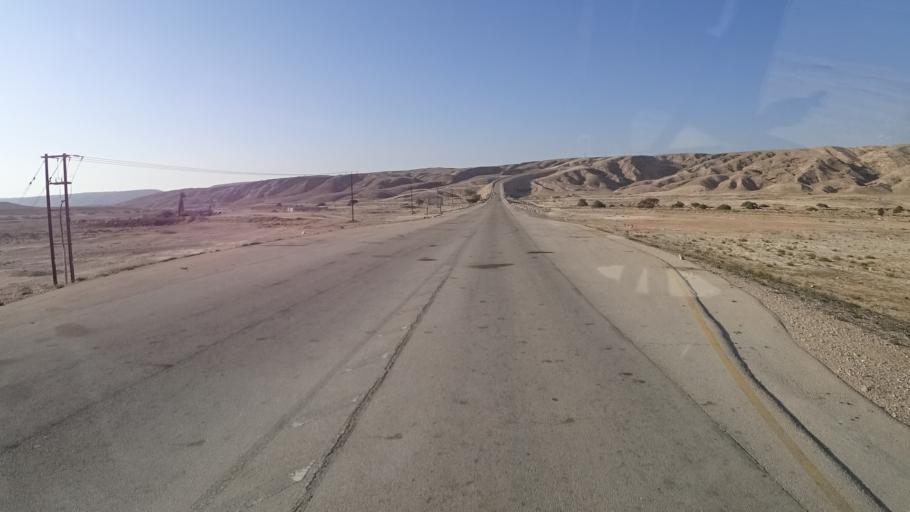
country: OM
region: Zufar
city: Salalah
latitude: 17.2393
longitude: 53.9174
